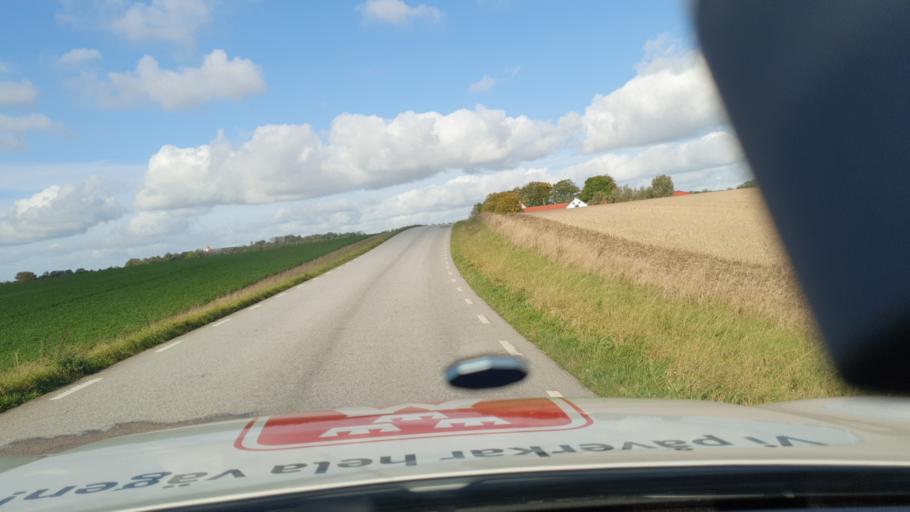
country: SE
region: Skane
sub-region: Ystads Kommun
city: Kopingebro
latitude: 55.4683
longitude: 14.0061
